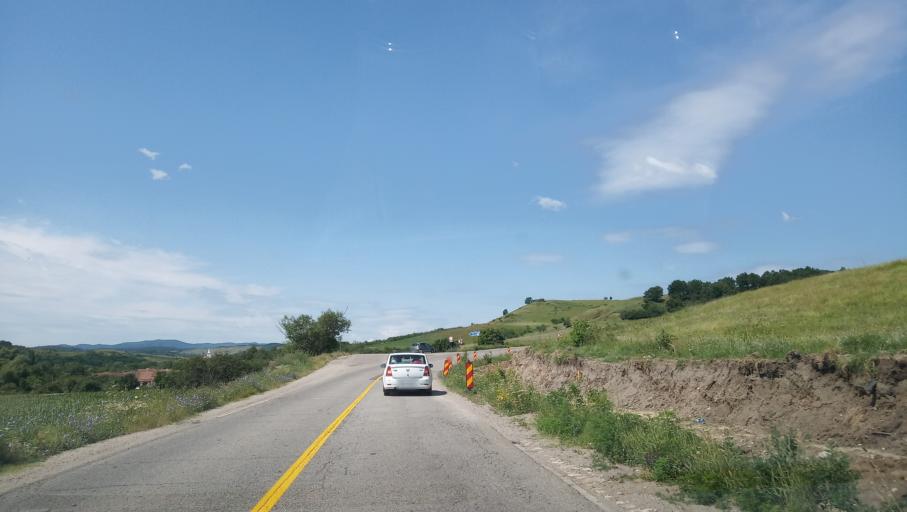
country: RO
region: Hunedoara
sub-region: Comuna Calan
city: Calan
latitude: 45.7260
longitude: 22.9672
